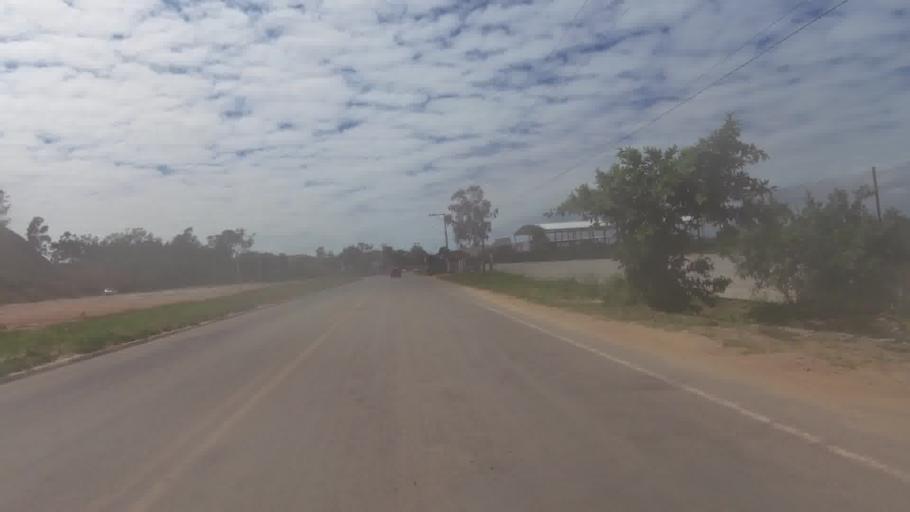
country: BR
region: Espirito Santo
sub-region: Marataizes
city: Marataizes
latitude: -21.2005
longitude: -40.9648
